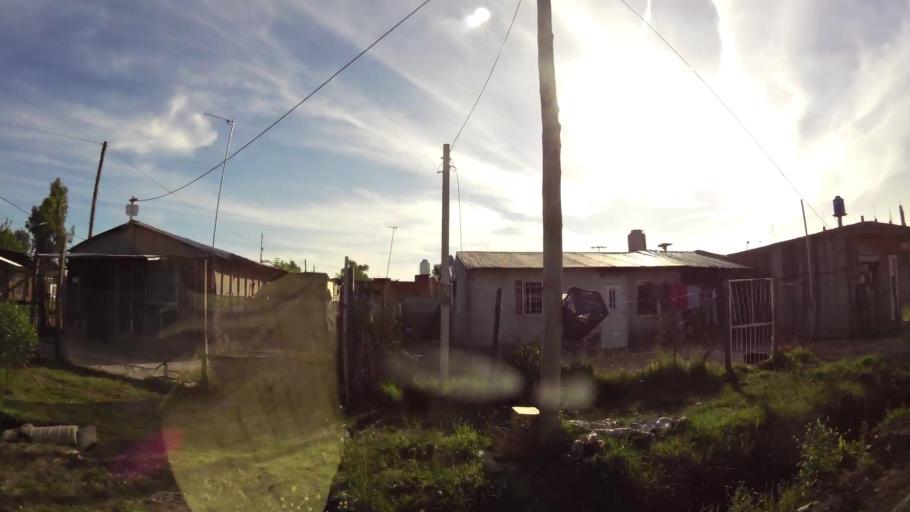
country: AR
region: Buenos Aires
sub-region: Partido de Almirante Brown
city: Adrogue
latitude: -34.8166
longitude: -58.3220
